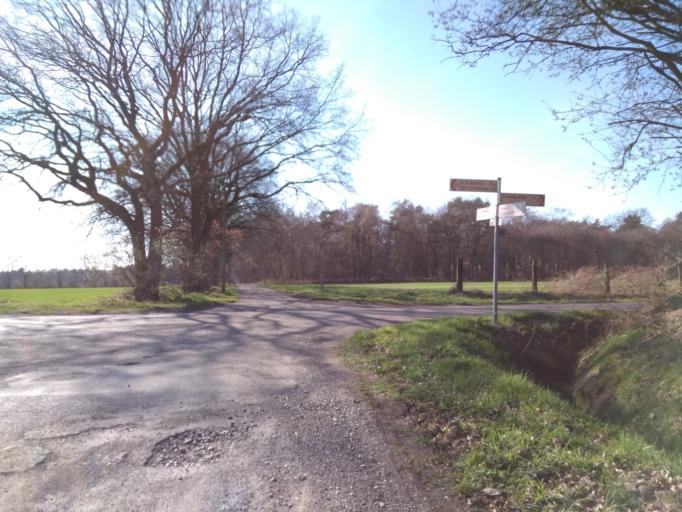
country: DE
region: North Rhine-Westphalia
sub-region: Regierungsbezirk Dusseldorf
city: Hunxe
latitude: 51.6139
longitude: 6.8442
